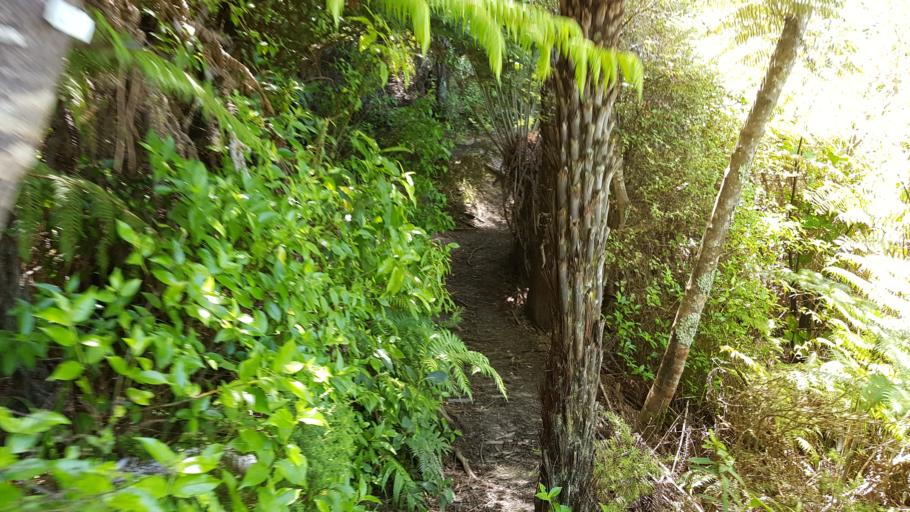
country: NZ
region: Auckland
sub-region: Auckland
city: North Shore
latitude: -36.8241
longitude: 174.7157
